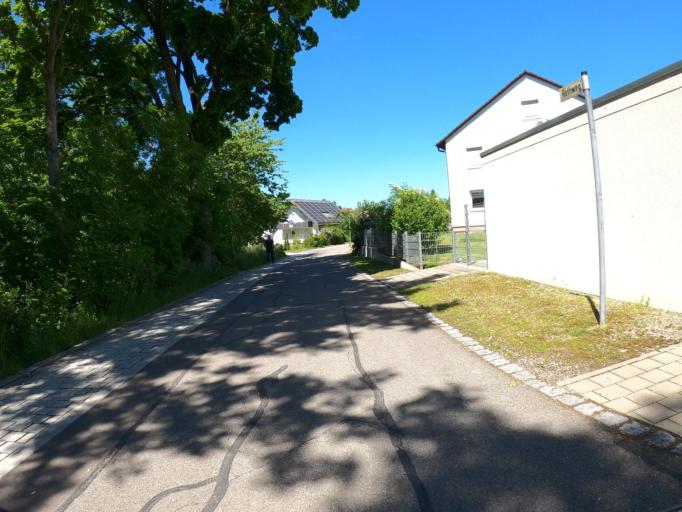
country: DE
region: Bavaria
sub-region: Swabia
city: Pfaffenhofen an der Roth
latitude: 48.3492
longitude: 10.1573
